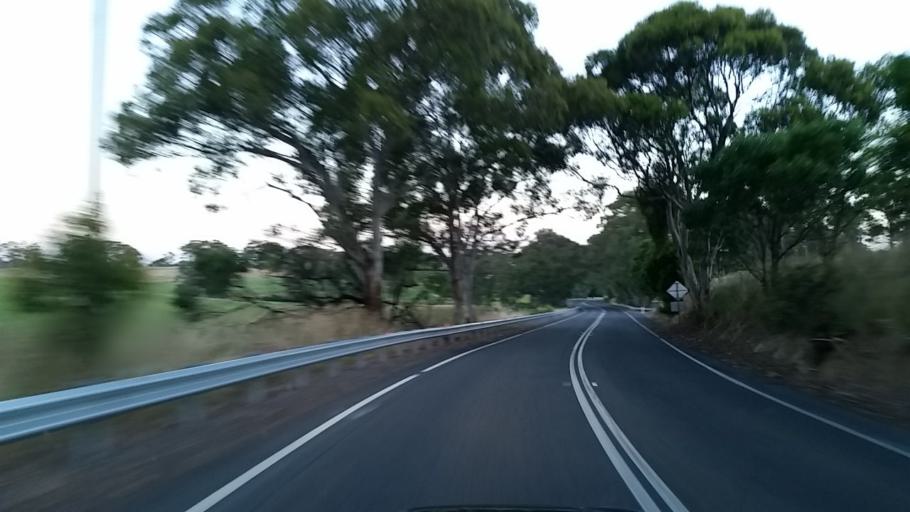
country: AU
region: South Australia
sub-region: Adelaide Hills
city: Lobethal
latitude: -34.8930
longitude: 138.8690
